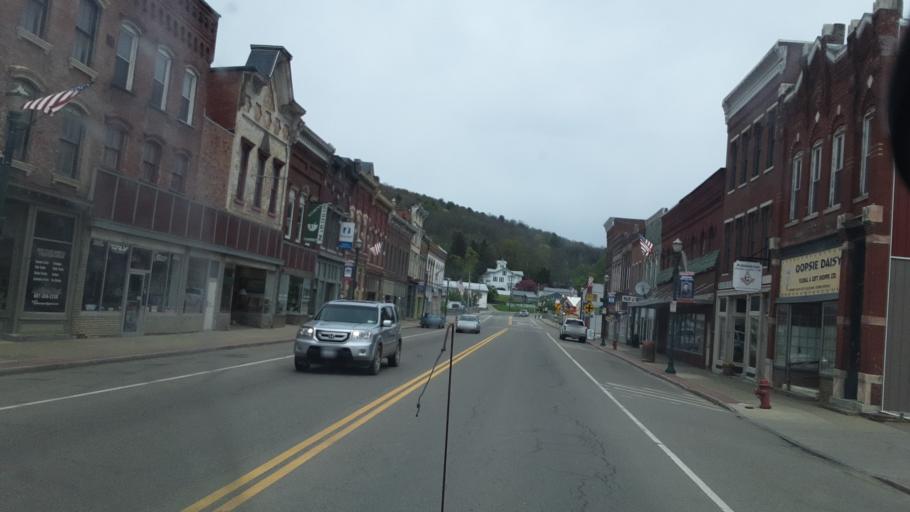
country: US
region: New York
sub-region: Steuben County
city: Addison
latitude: 42.1057
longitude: -77.2341
